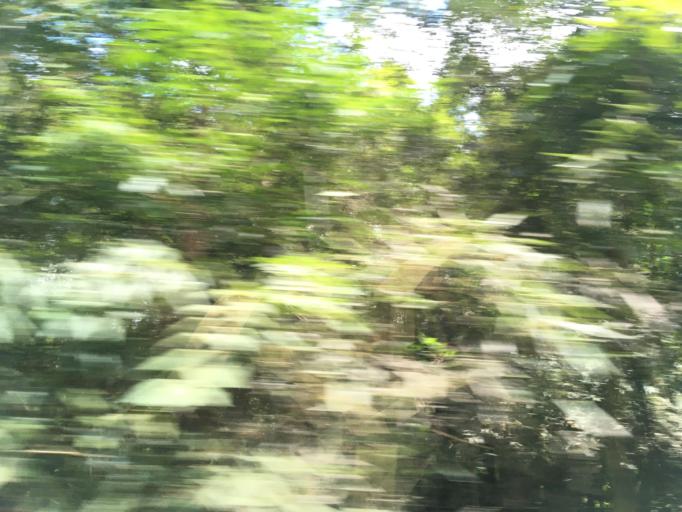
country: TW
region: Taipei
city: Taipei
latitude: 24.9383
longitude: 121.5789
